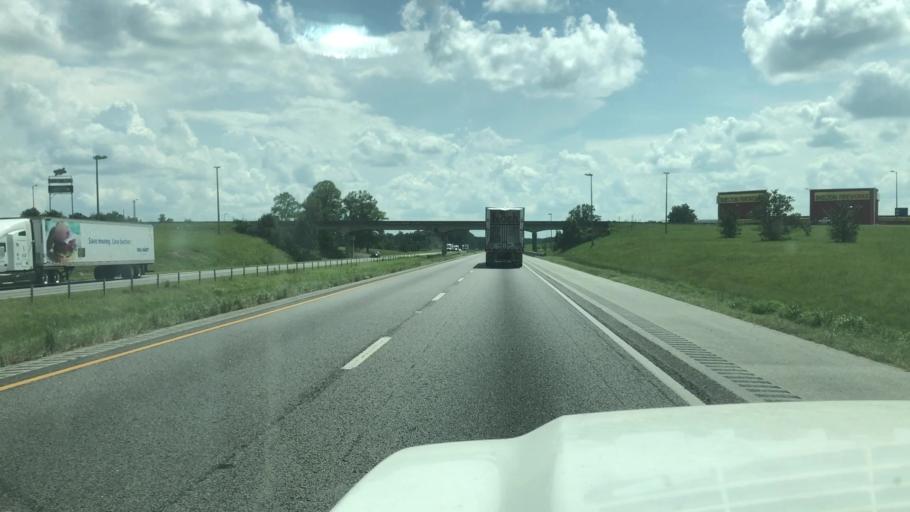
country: US
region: Alabama
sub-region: Chambers County
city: Huguley
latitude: 32.7477
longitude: -85.2800
